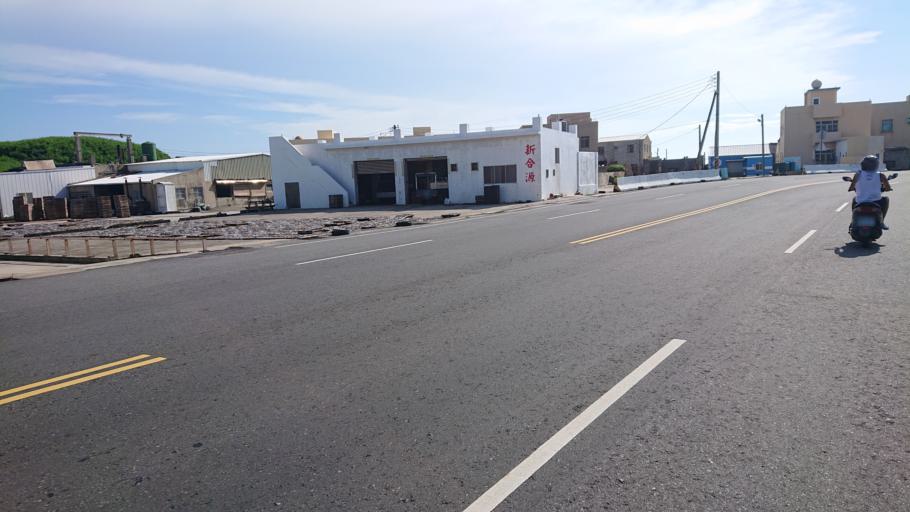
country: TW
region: Taiwan
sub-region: Penghu
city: Ma-kung
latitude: 23.5194
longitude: 119.5754
